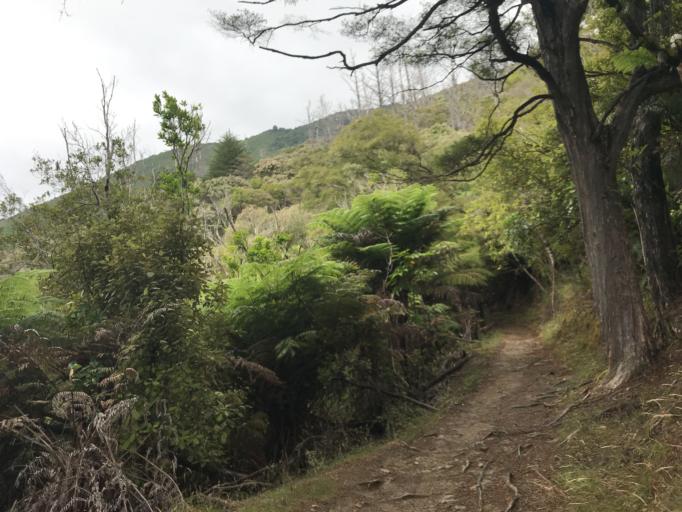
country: NZ
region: Marlborough
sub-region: Marlborough District
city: Picton
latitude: -41.2284
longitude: 173.9586
